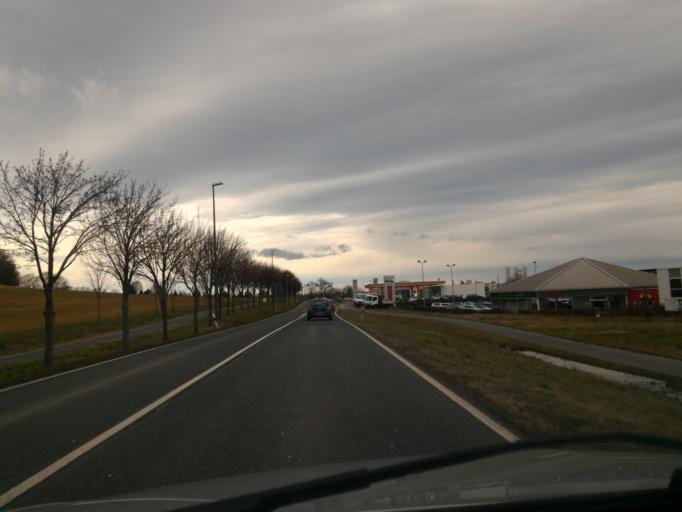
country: DE
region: Saxony
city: Radeberg
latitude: 51.0643
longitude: 13.8983
